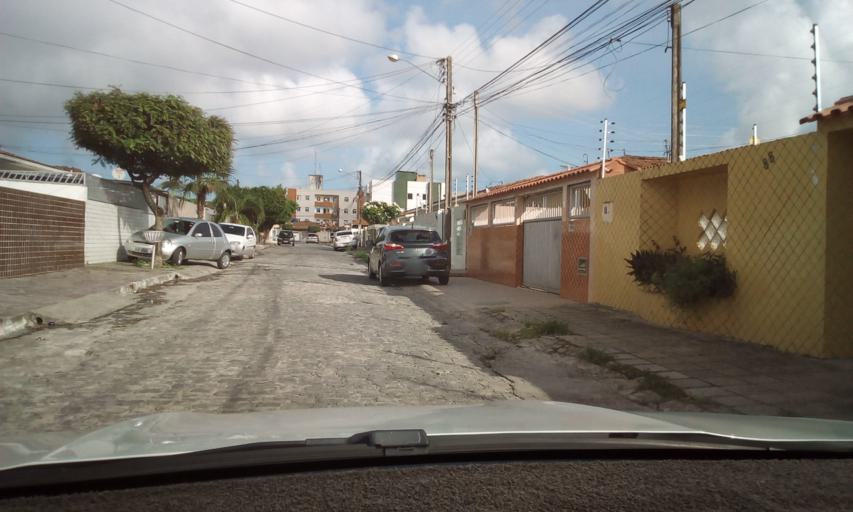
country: BR
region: Paraiba
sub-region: Joao Pessoa
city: Joao Pessoa
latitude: -7.1673
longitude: -34.8617
